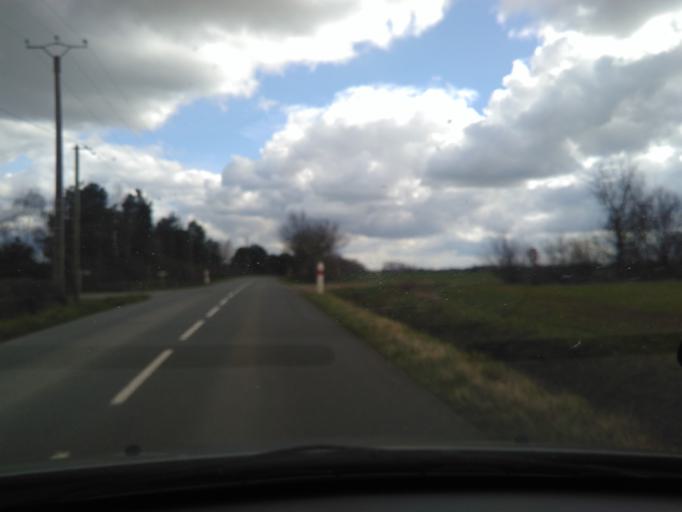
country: FR
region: Pays de la Loire
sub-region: Departement de la Vendee
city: Saint-Martin-des-Noyers
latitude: 46.7018
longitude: -1.1445
